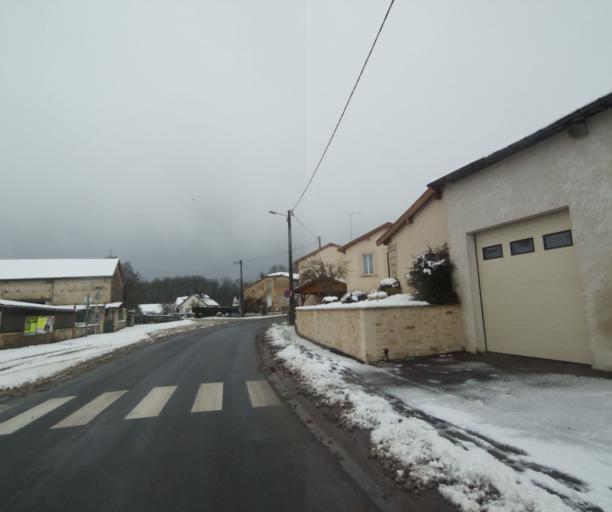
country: FR
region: Champagne-Ardenne
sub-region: Departement de la Haute-Marne
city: Wassy
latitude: 48.4398
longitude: 4.9584
